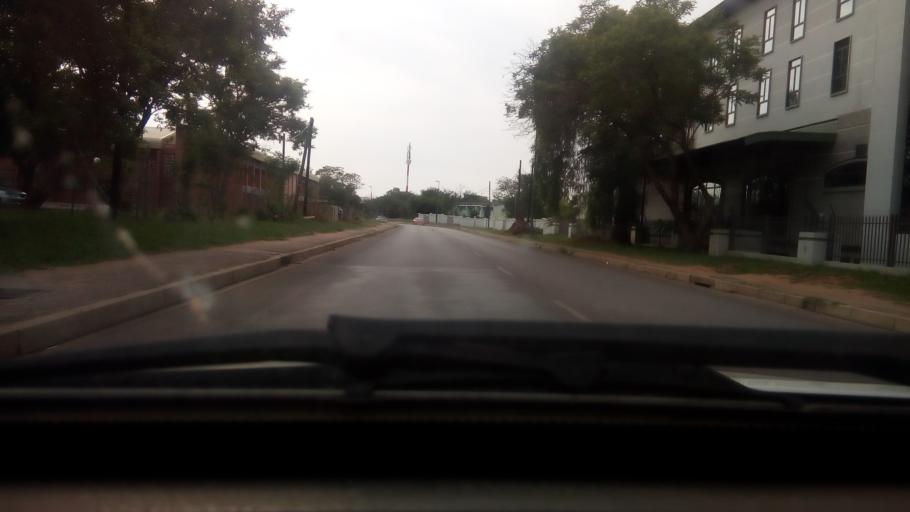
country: BW
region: South East
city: Gaborone
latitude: -24.6670
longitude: 25.9367
